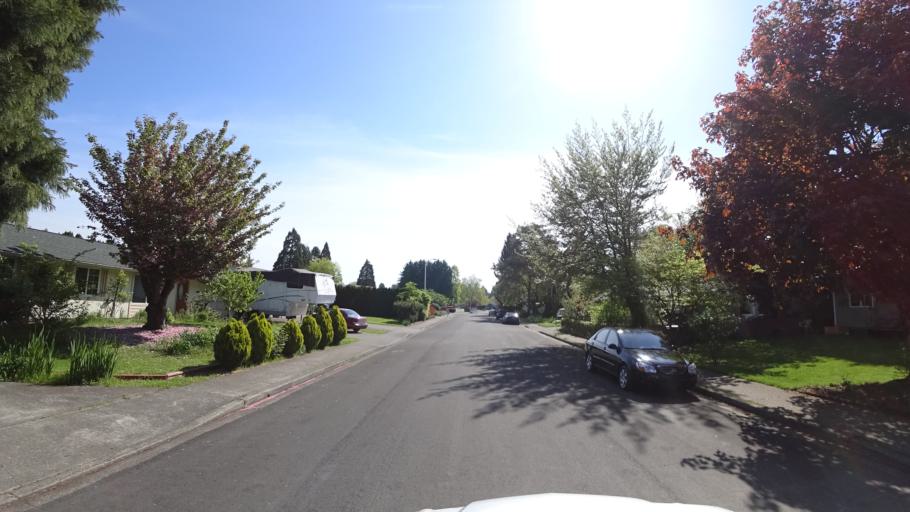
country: US
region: Oregon
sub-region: Washington County
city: Hillsboro
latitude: 45.5261
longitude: -122.9459
